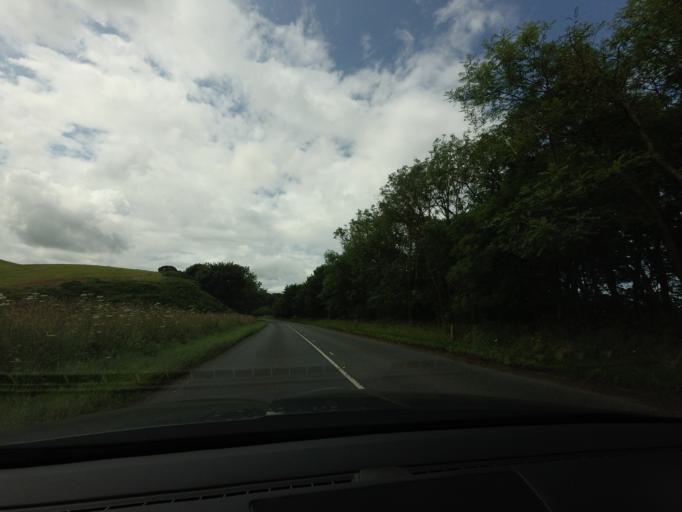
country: GB
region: Scotland
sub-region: Aberdeenshire
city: Whitehills
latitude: 57.6649
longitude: -2.5705
